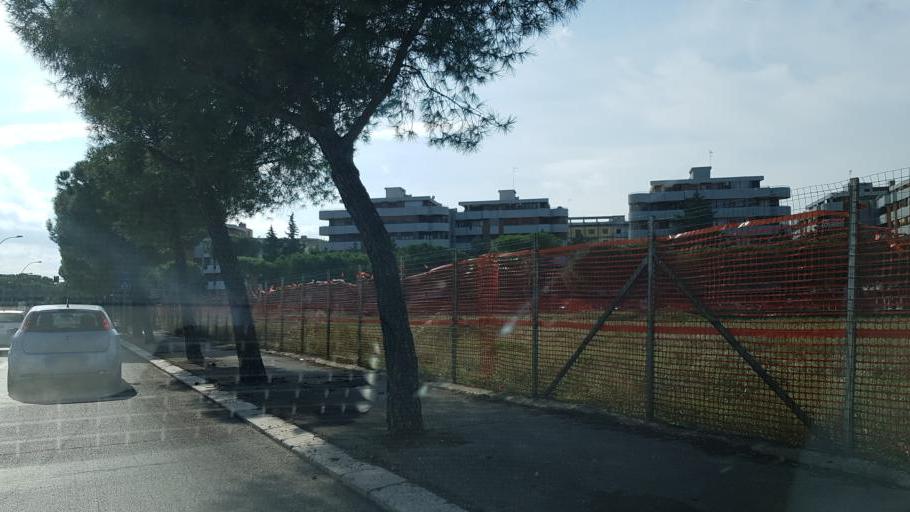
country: IT
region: Apulia
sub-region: Provincia di Foggia
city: Foggia
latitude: 41.4562
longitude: 15.5642
